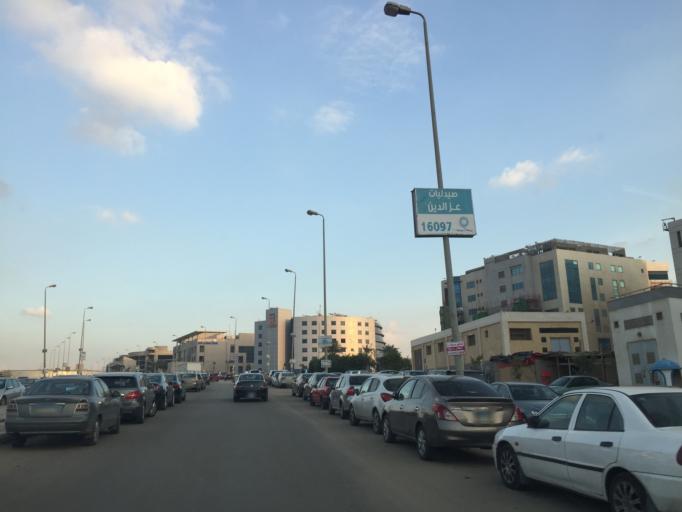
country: EG
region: Muhafazat al Qahirah
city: Cairo
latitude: 30.0181
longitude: 31.4242
